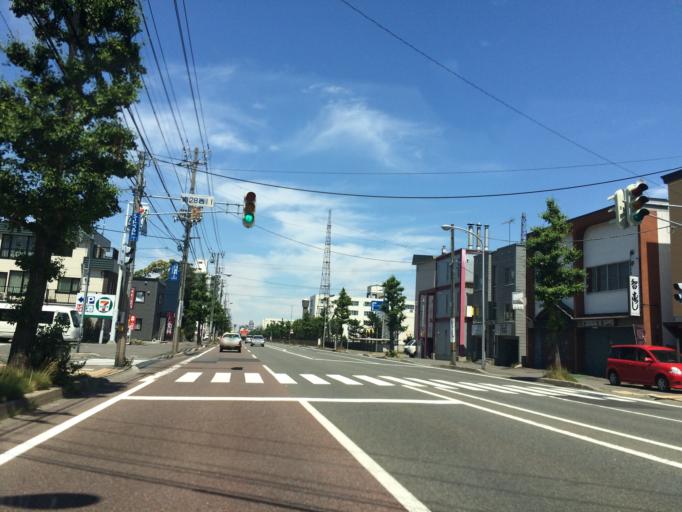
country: JP
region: Hokkaido
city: Sapporo
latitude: 43.0213
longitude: 141.3460
